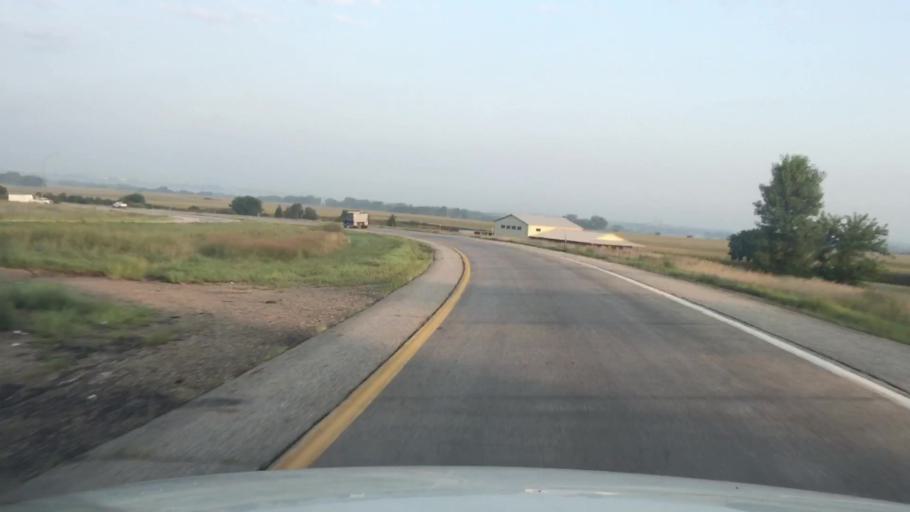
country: US
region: Iowa
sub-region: Polk County
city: Altoona
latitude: 41.6607
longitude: -93.5224
